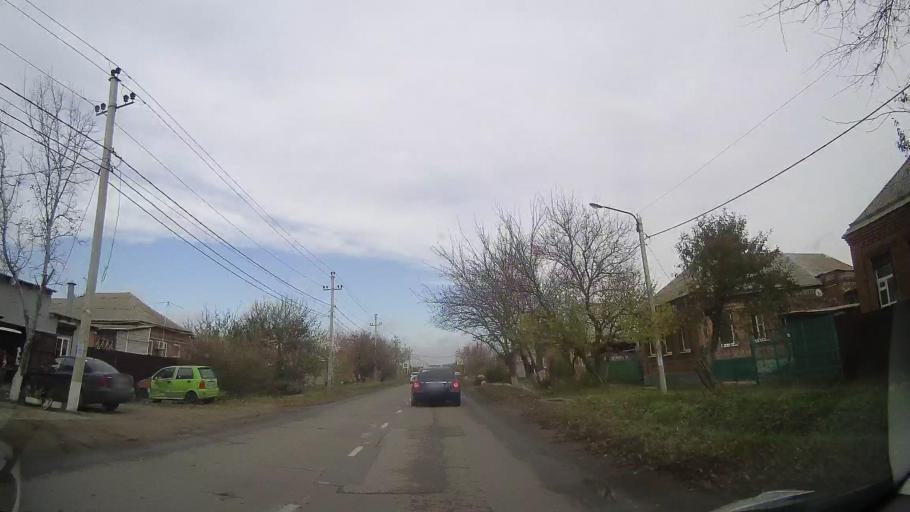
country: RU
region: Rostov
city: Bataysk
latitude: 47.1462
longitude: 39.7670
